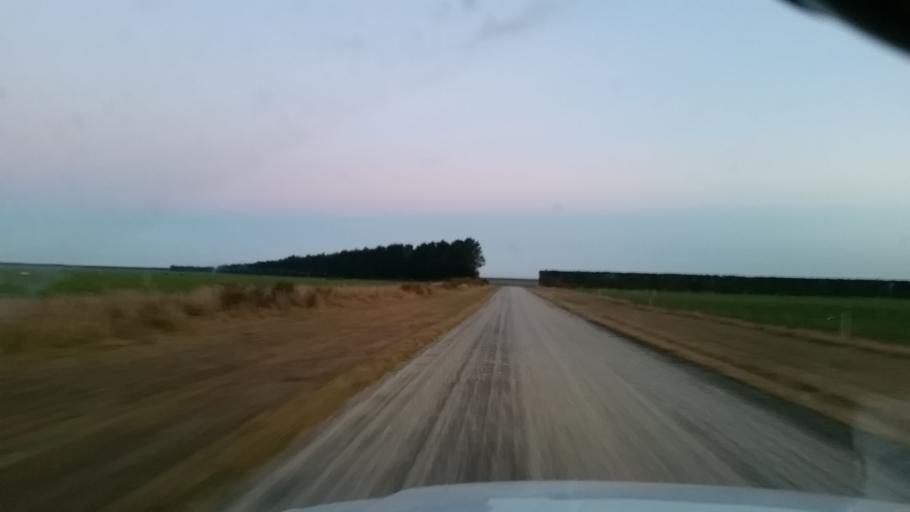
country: NZ
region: Canterbury
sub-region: Ashburton District
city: Tinwald
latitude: -43.9432
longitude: 171.6104
